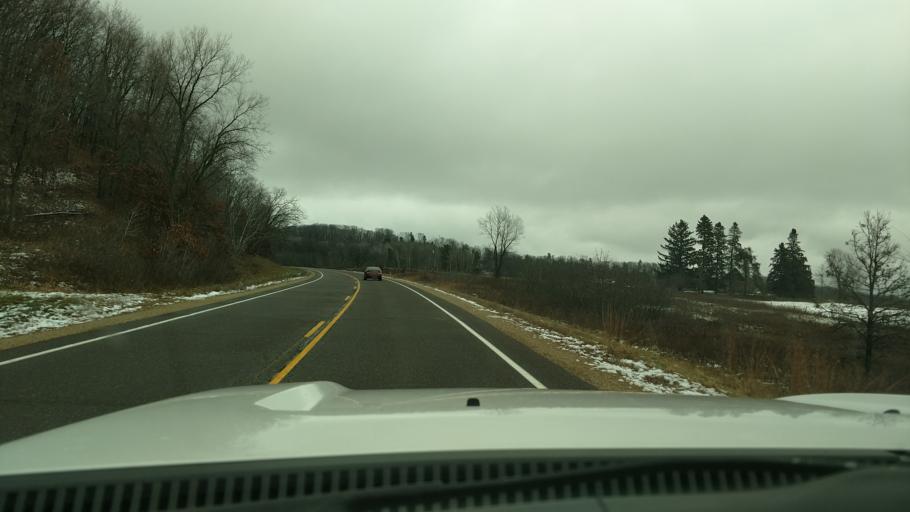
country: US
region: Wisconsin
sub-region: Dunn County
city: Boyceville
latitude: 45.1293
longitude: -92.0028
